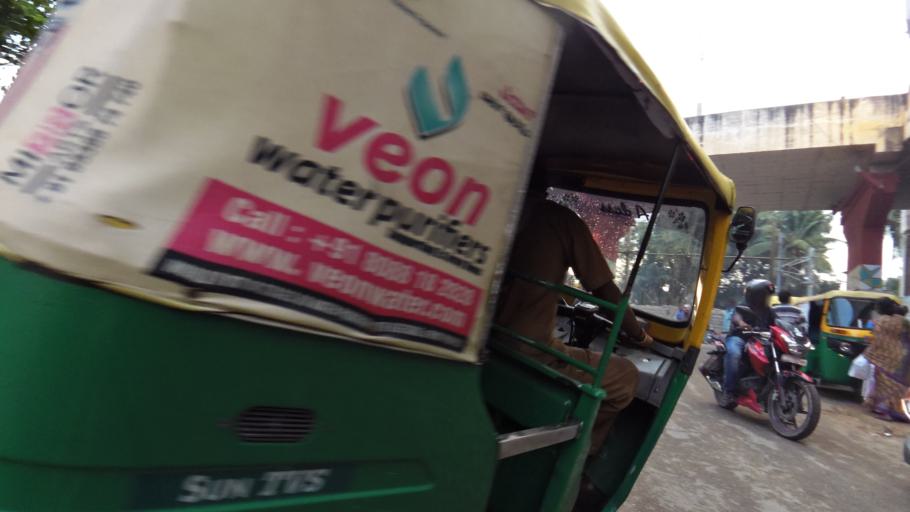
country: IN
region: Karnataka
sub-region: Bangalore Urban
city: Bangalore
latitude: 13.0038
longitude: 77.6364
